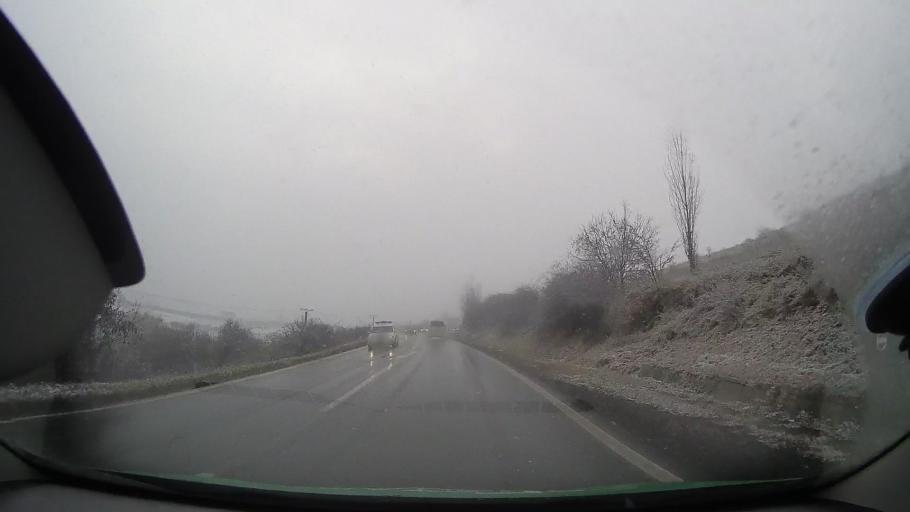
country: RO
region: Mures
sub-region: Comuna Bagaciu
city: Delenii
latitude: 46.2610
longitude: 24.3014
